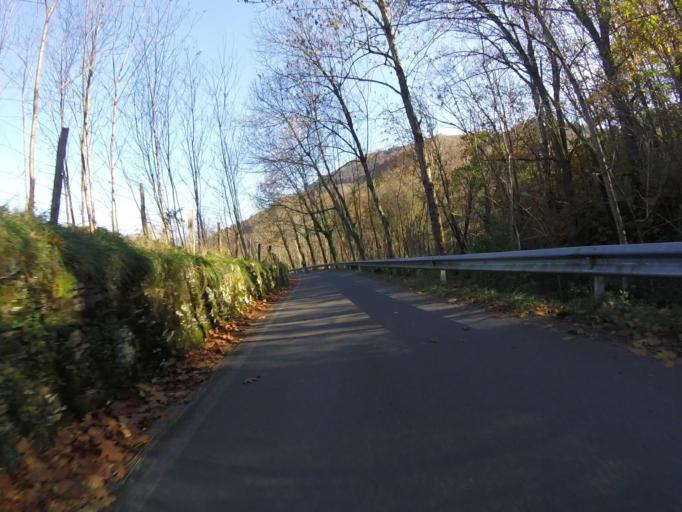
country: ES
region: Navarre
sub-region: Provincia de Navarra
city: Igantzi
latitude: 43.2328
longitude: -1.7024
